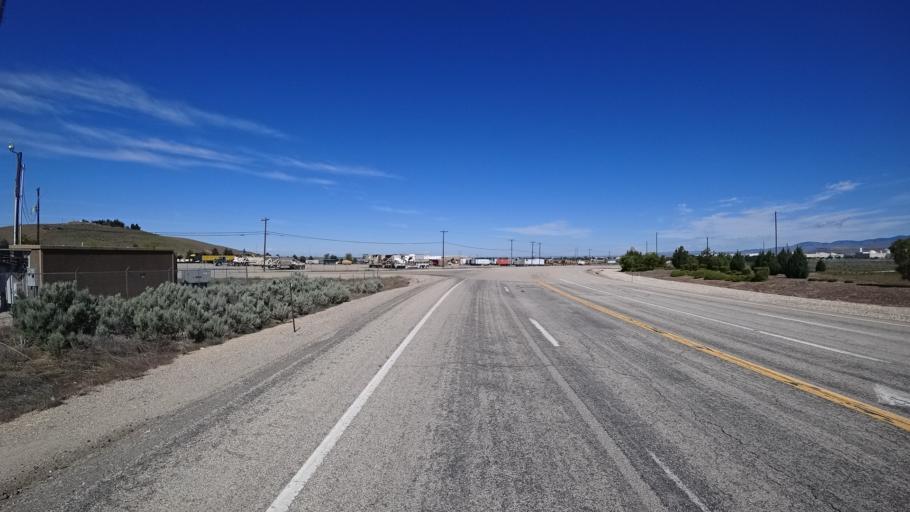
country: US
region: Idaho
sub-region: Ada County
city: Boise
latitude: 43.5115
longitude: -116.1419
